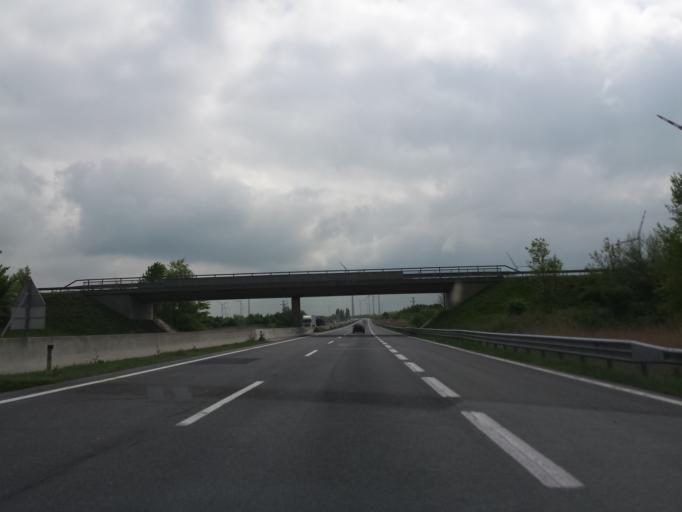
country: AT
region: Burgenland
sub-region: Politischer Bezirk Neusiedl am See
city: Zurndorf
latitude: 47.9328
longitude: 16.9959
